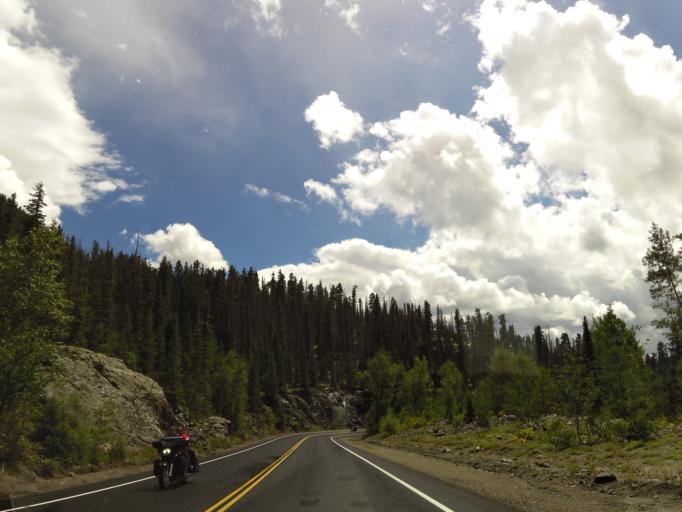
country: US
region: Colorado
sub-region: San Juan County
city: Silverton
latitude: 37.6769
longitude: -107.7805
